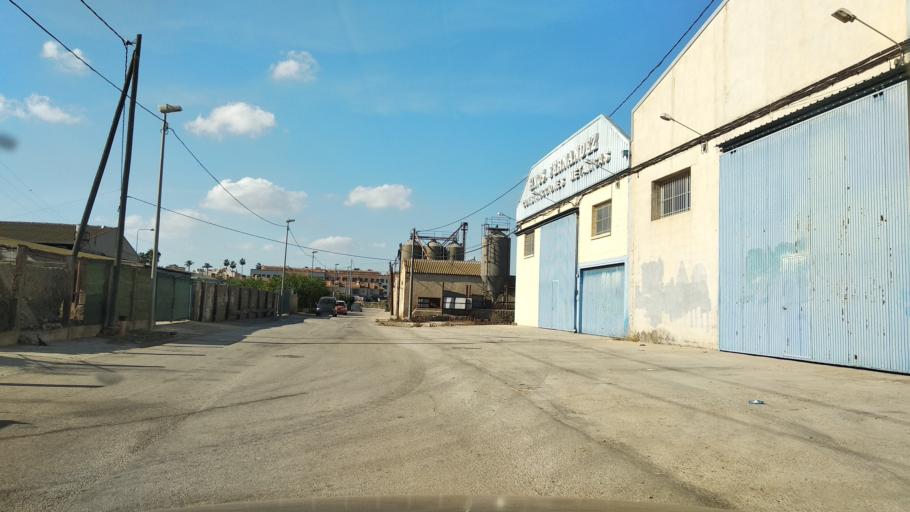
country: ES
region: Murcia
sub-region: Murcia
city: Santomera
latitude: 38.0564
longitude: -1.0435
